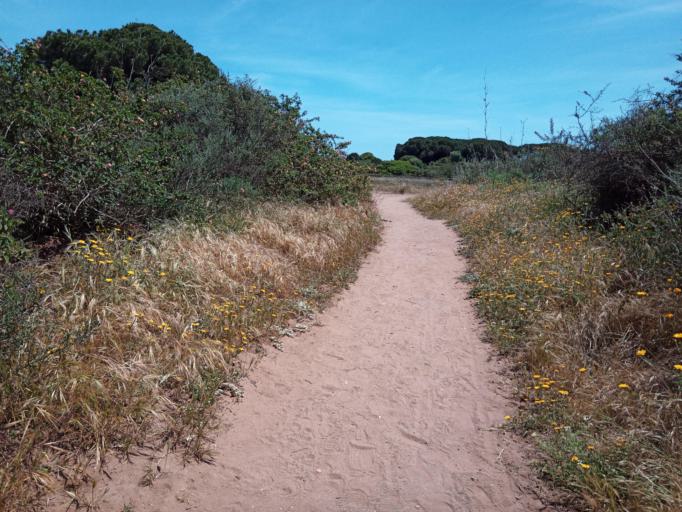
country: ES
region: Andalusia
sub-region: Provincia de Malaga
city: Ojen
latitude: 36.4879
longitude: -4.7513
